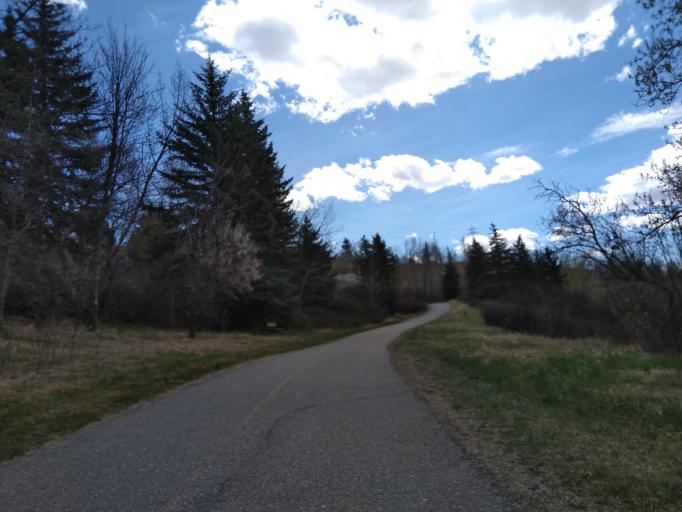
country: CA
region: Alberta
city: Calgary
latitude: 51.0841
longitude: -114.1655
